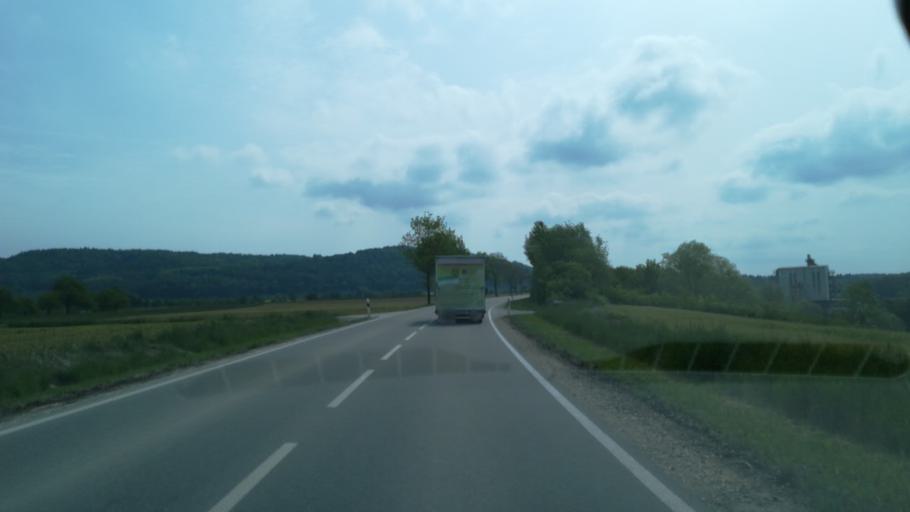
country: DE
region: Baden-Wuerttemberg
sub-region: Freiburg Region
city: Steisslingen
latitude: 47.7838
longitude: 8.9180
